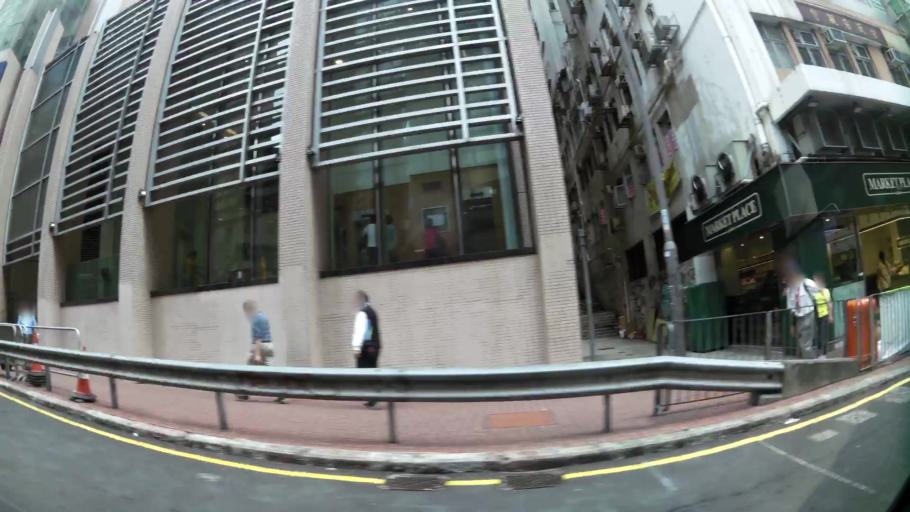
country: HK
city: Hong Kong
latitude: 22.2847
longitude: 114.1511
